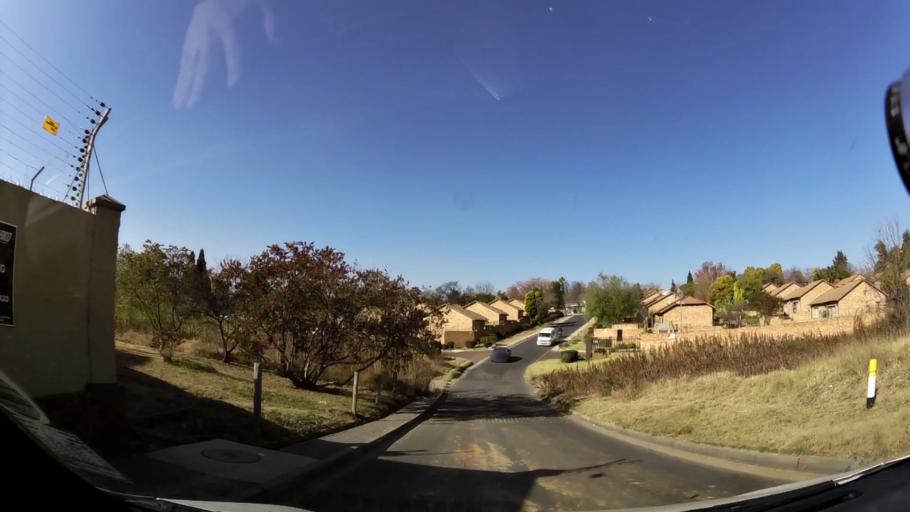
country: ZA
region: Gauteng
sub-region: City of Johannesburg Metropolitan Municipality
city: Diepsloot
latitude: -26.0257
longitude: 27.9753
